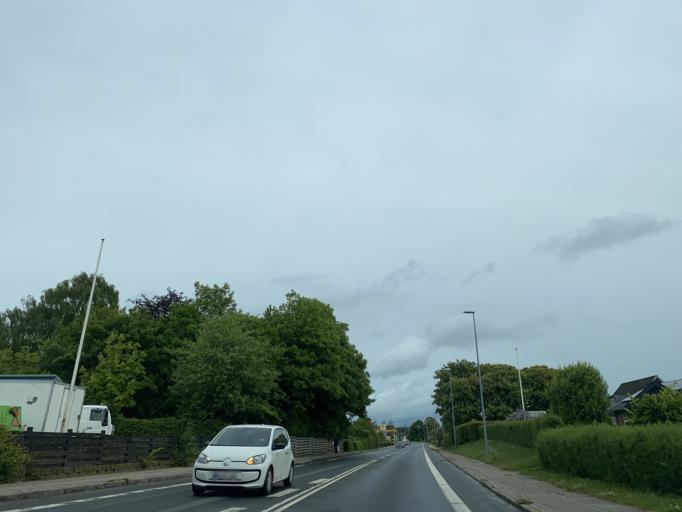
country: DK
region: Central Jutland
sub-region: Favrskov Kommune
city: Hammel
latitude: 56.2498
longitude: 9.8591
